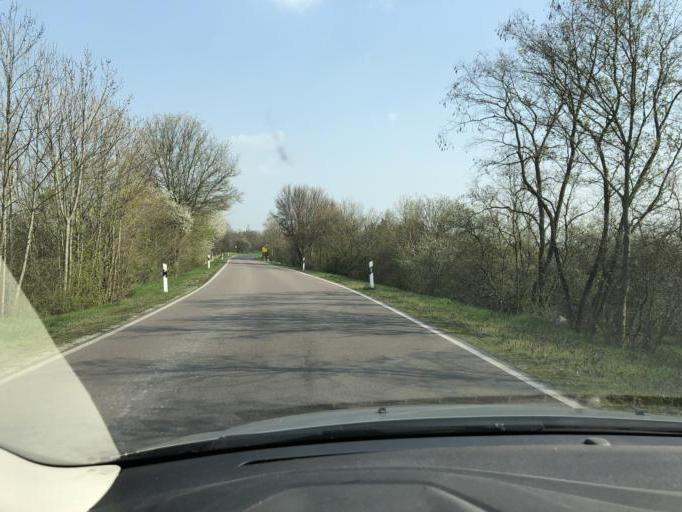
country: DE
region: Saxony-Anhalt
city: Niemberg
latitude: 51.5536
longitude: 12.0810
